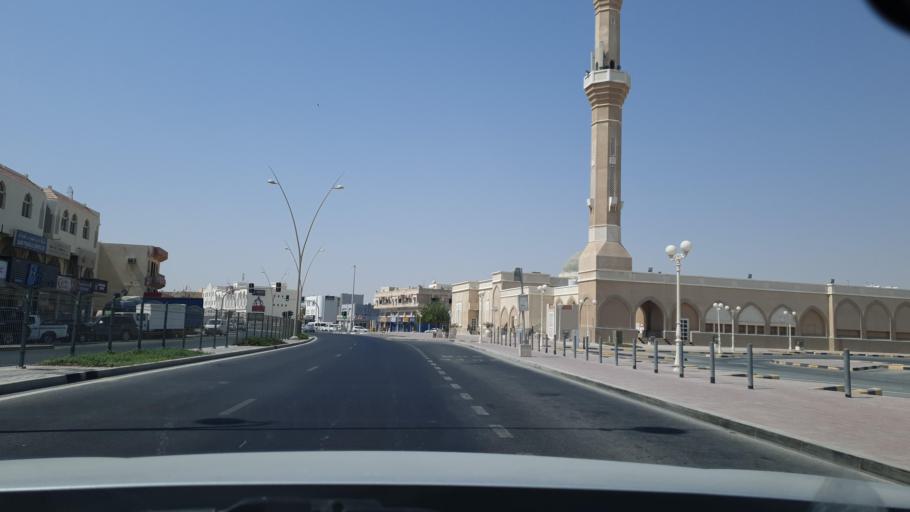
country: QA
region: Al Khawr
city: Al Khawr
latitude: 25.6843
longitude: 51.5078
